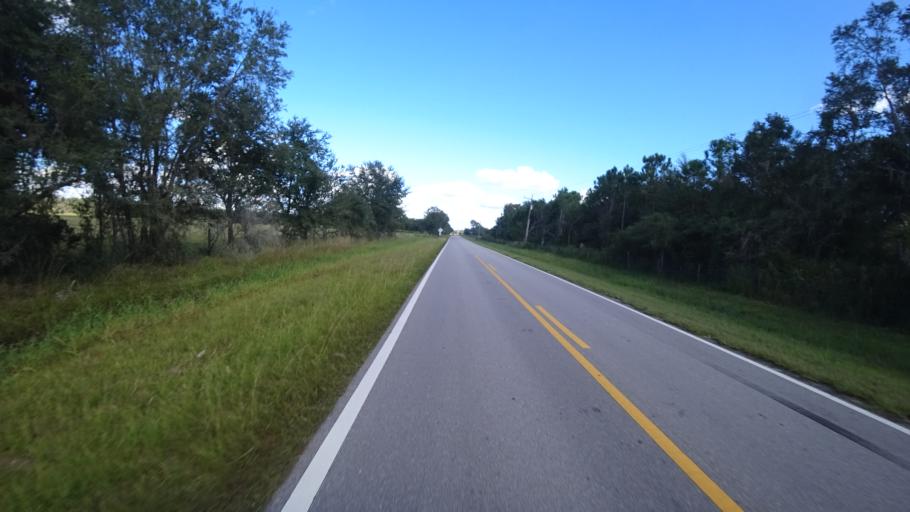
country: US
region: Florida
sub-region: Sarasota County
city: Lake Sarasota
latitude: 27.2889
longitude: -82.2321
